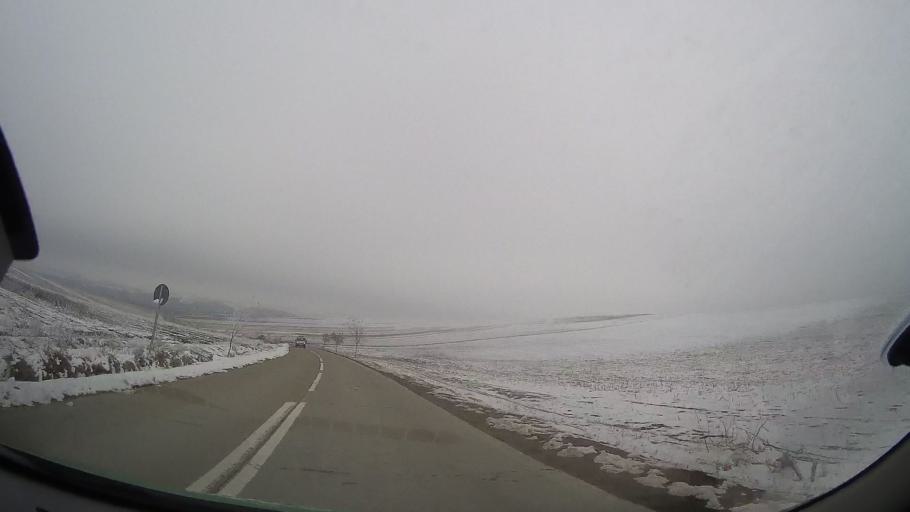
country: RO
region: Vaslui
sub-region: Comuna Ivesti
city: Ivesti
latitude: 46.2024
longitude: 27.5085
